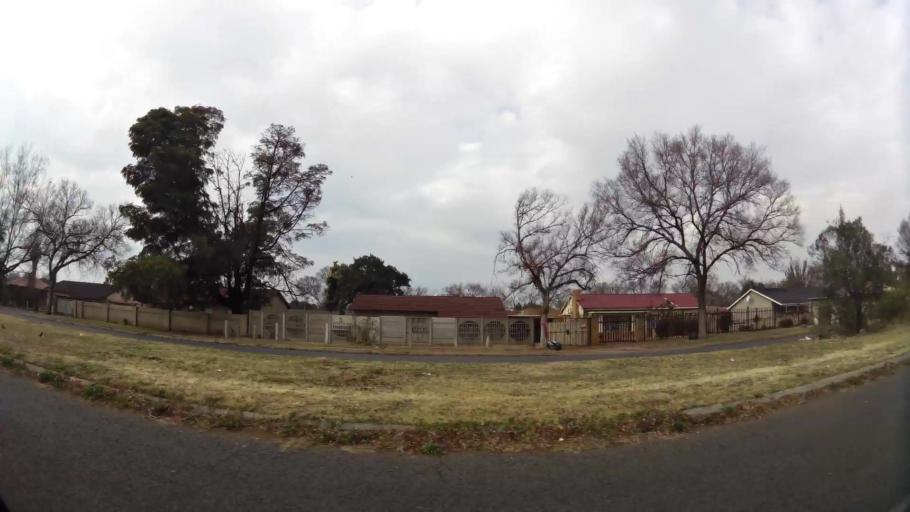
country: ZA
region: Gauteng
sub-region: Sedibeng District Municipality
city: Vanderbijlpark
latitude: -26.6848
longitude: 27.8301
